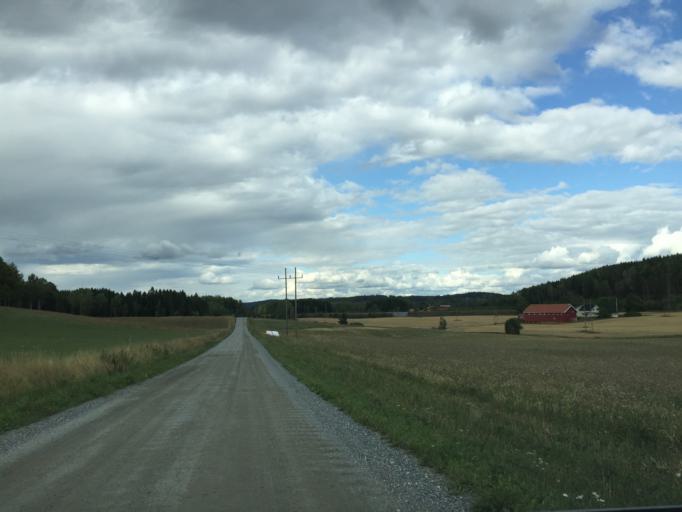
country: NO
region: Ostfold
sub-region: Askim
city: Askim
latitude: 59.5965
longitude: 11.1347
